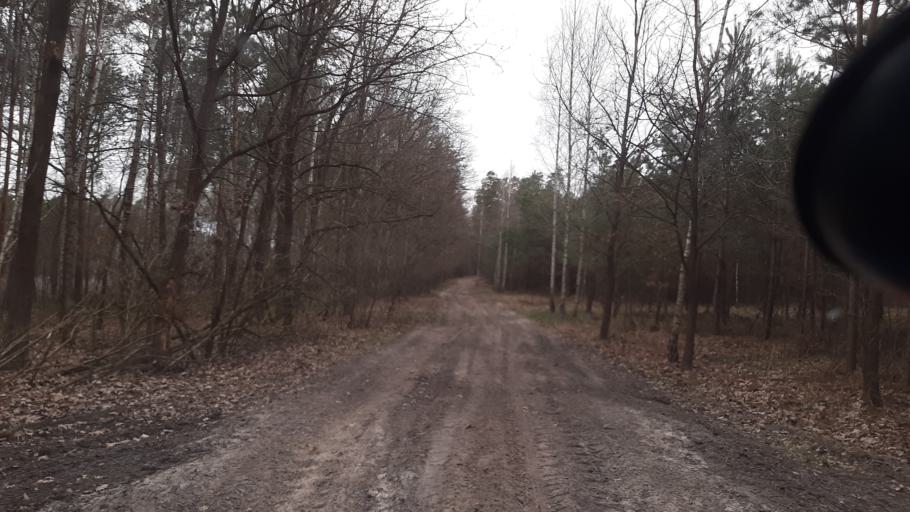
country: PL
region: Lublin Voivodeship
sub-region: Powiat lubelski
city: Garbow
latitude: 51.4012
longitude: 22.3695
